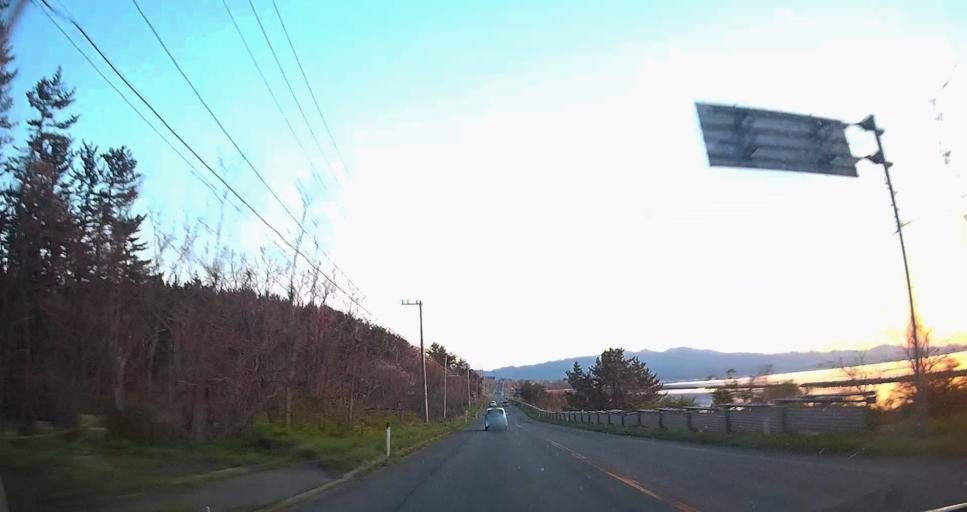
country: JP
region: Aomori
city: Misawa
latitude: 40.8827
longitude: 141.1551
